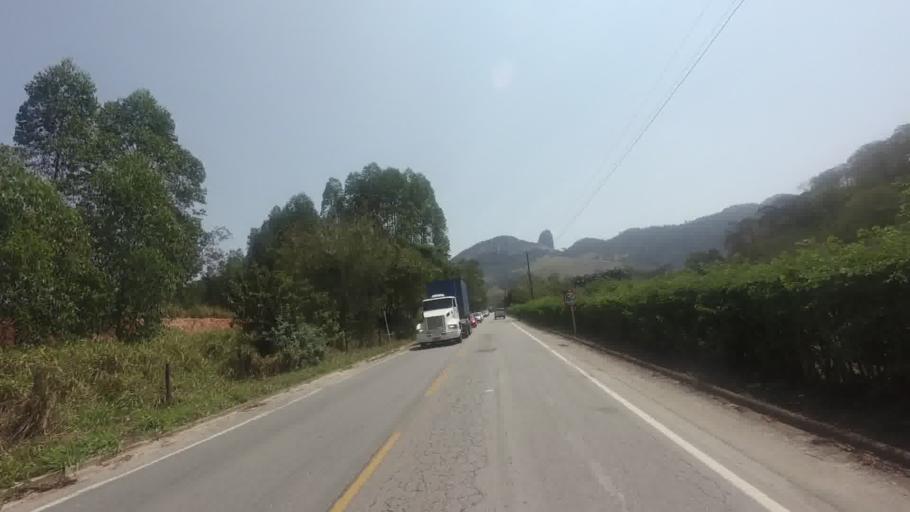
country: BR
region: Espirito Santo
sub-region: Cachoeiro De Itapemirim
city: Cachoeiro de Itapemirim
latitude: -20.8607
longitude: -41.0496
